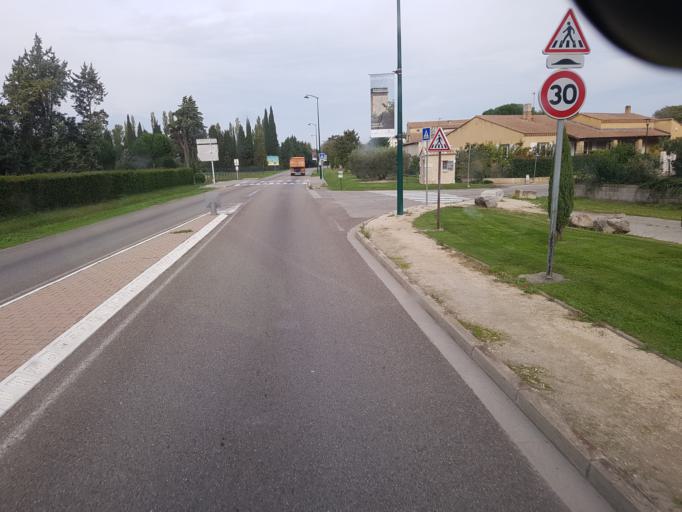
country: FR
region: Provence-Alpes-Cote d'Azur
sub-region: Departement des Bouches-du-Rhone
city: Barbentane
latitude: 43.9004
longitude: 4.7426
